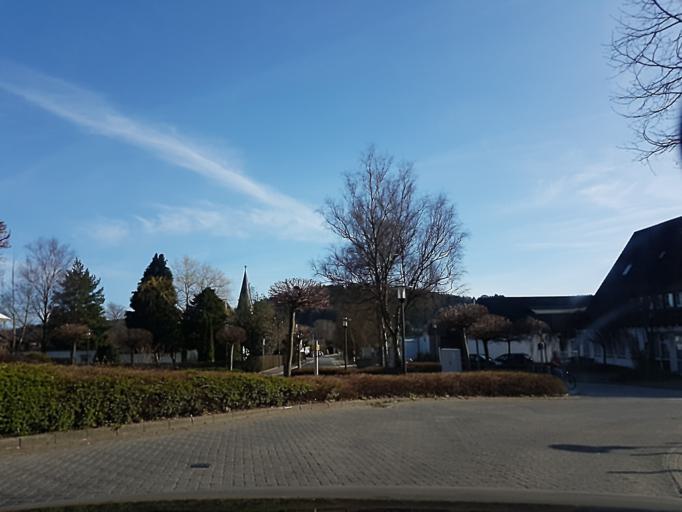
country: DE
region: North Rhine-Westphalia
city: Kierspe
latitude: 51.1281
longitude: 7.6004
